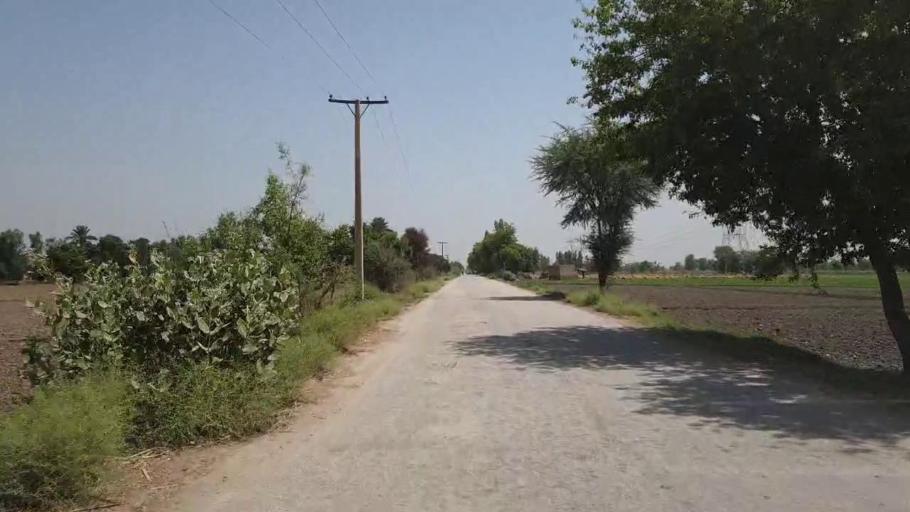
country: PK
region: Sindh
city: Adilpur
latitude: 27.8317
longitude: 69.2557
